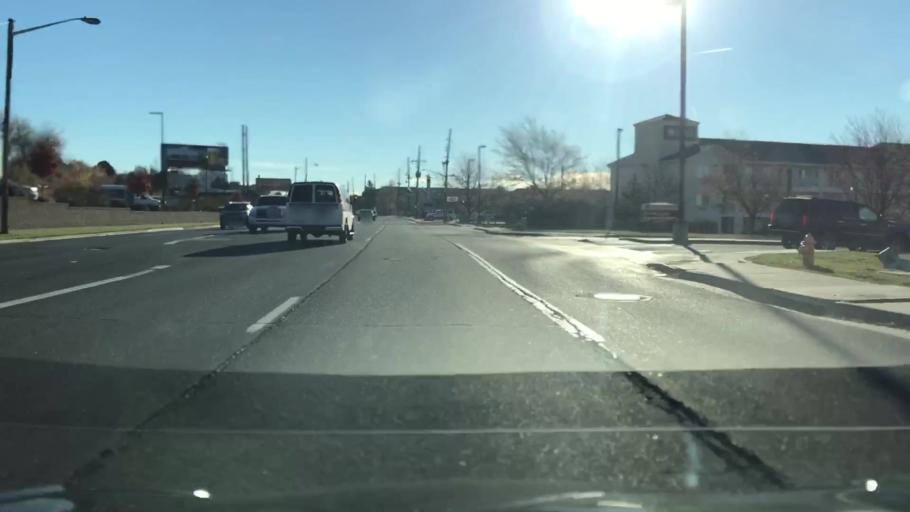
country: US
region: Colorado
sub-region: Arapahoe County
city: Glendale
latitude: 39.7091
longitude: -104.9318
